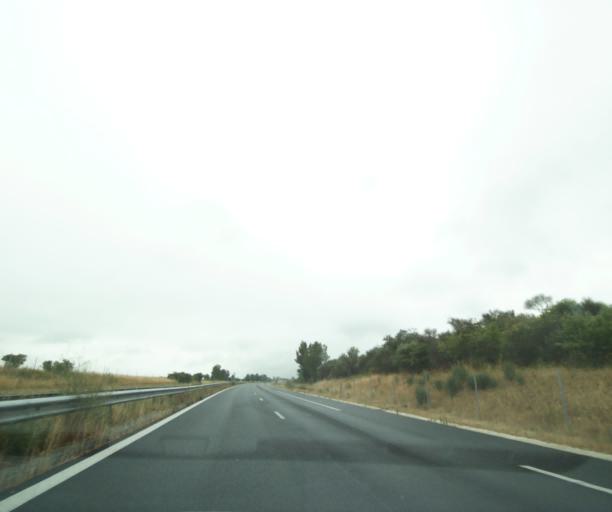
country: FR
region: Midi-Pyrenees
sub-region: Departement du Tarn
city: Lisle-sur-Tarn
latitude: 43.8363
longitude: 1.8353
